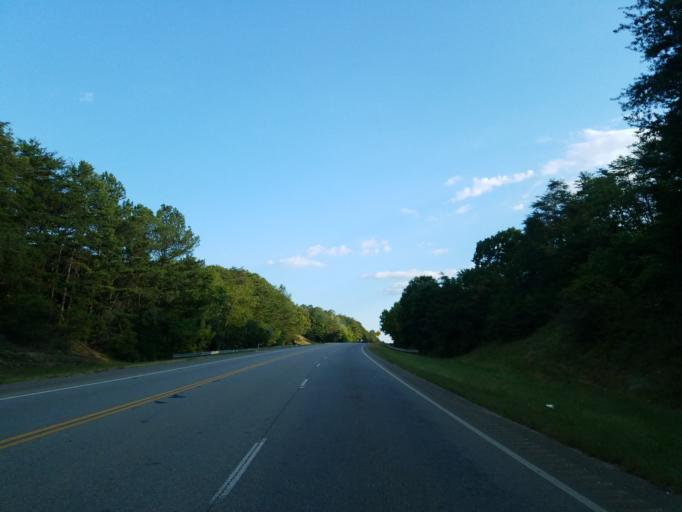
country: US
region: Georgia
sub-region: Murray County
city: Chatsworth
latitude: 34.6865
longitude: -84.7307
